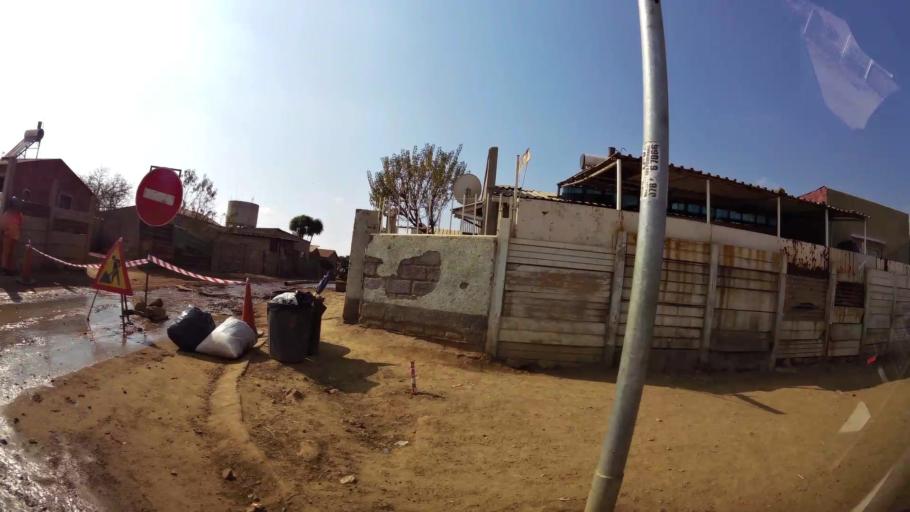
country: ZA
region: Gauteng
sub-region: Ekurhuleni Metropolitan Municipality
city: Springs
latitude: -26.1116
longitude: 28.4853
